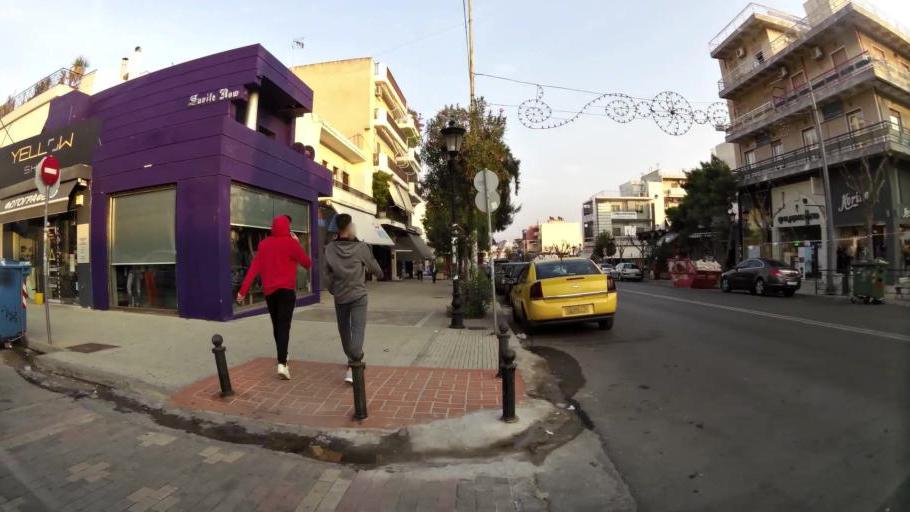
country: GR
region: Attica
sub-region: Nomarchia Athinas
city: Petroupolis
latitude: 38.0403
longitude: 23.6884
